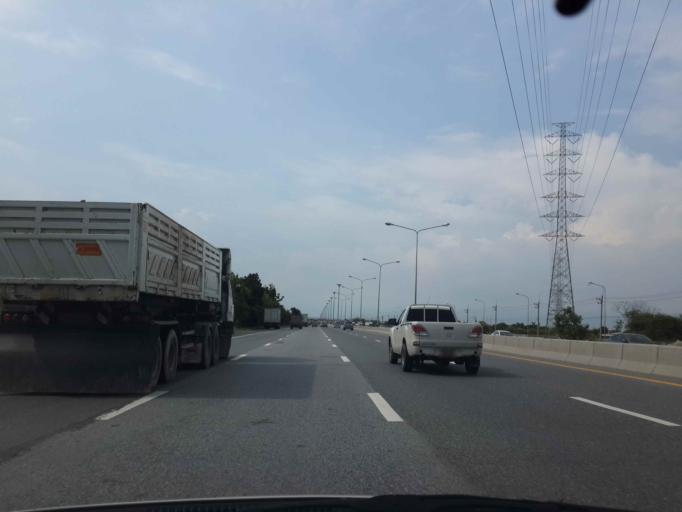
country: TH
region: Chon Buri
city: Phan Thong
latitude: 13.4491
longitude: 101.0460
